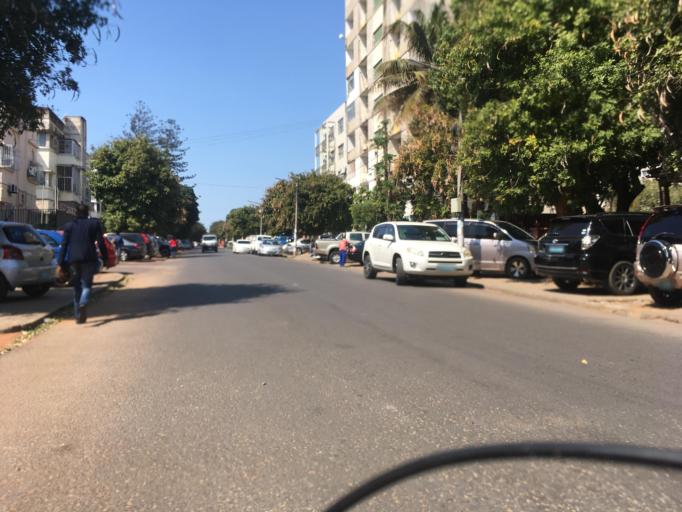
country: MZ
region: Maputo City
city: Maputo
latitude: -25.9660
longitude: 32.5768
